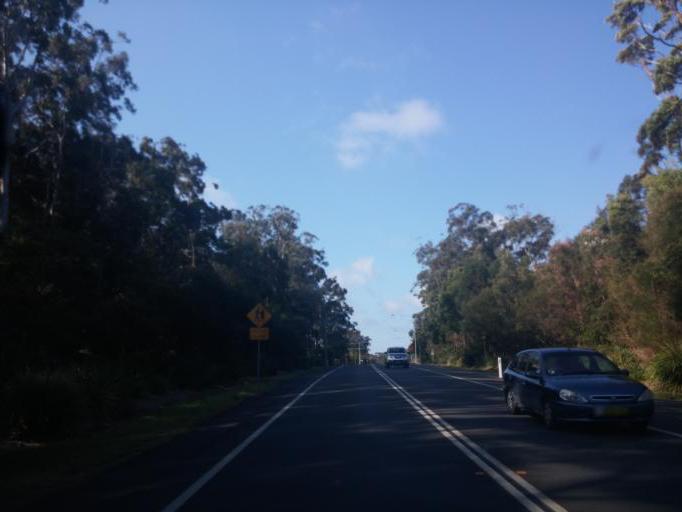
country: AU
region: New South Wales
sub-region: Coffs Harbour
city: Coffs Harbour
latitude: -30.2972
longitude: 153.1285
